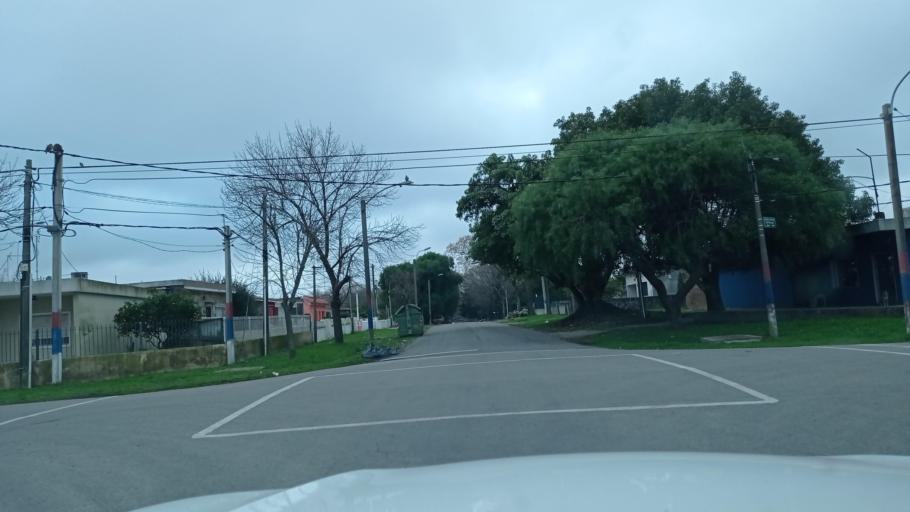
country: UY
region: Canelones
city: La Paz
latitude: -34.8364
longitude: -56.2290
